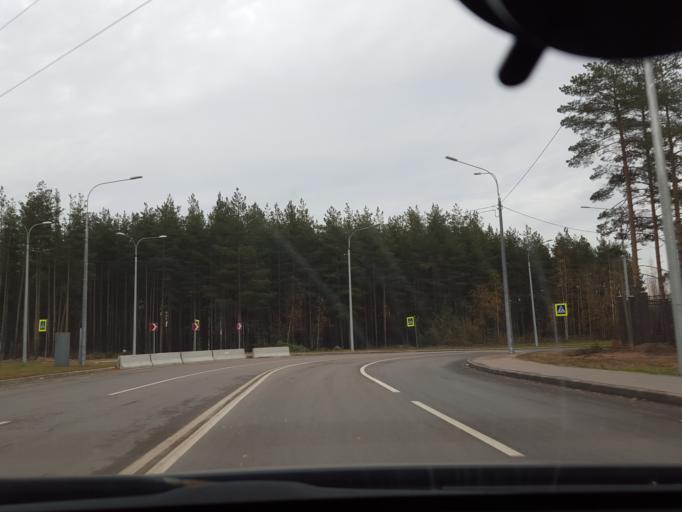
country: RU
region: Leningrad
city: Untolovo
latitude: 60.0493
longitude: 30.2367
